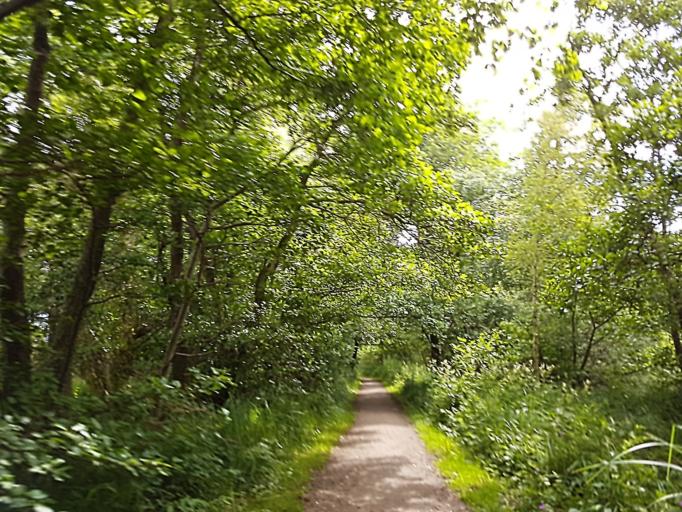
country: DK
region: Capital Region
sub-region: Fureso Kommune
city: Farum
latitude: 55.8056
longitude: 12.3345
